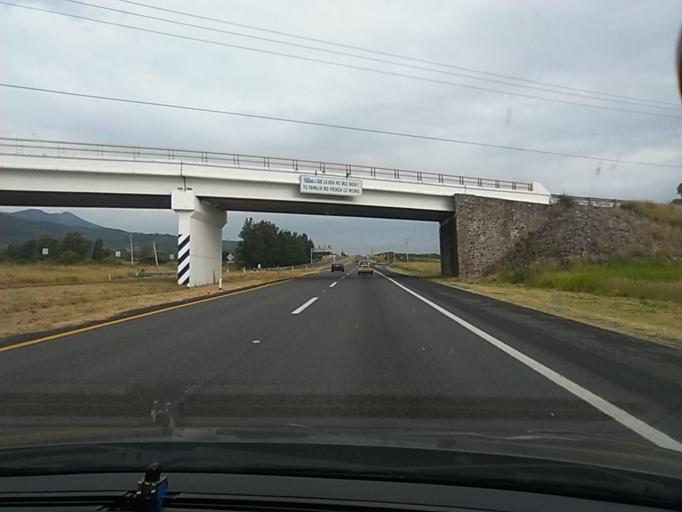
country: MX
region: Michoacan
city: Churintzio
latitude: 20.1324
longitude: -102.0697
